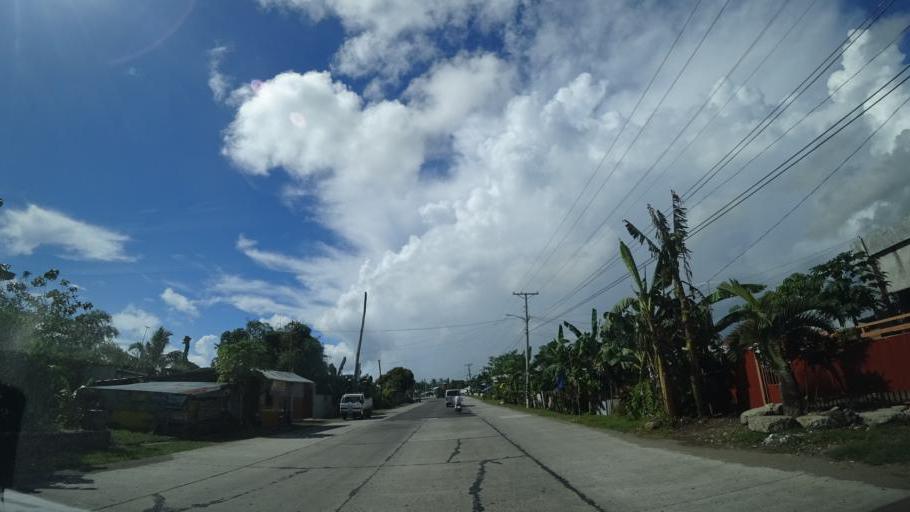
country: PH
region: Eastern Visayas
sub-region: Province of Leyte
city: Tanauan
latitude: 11.1296
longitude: 125.0086
